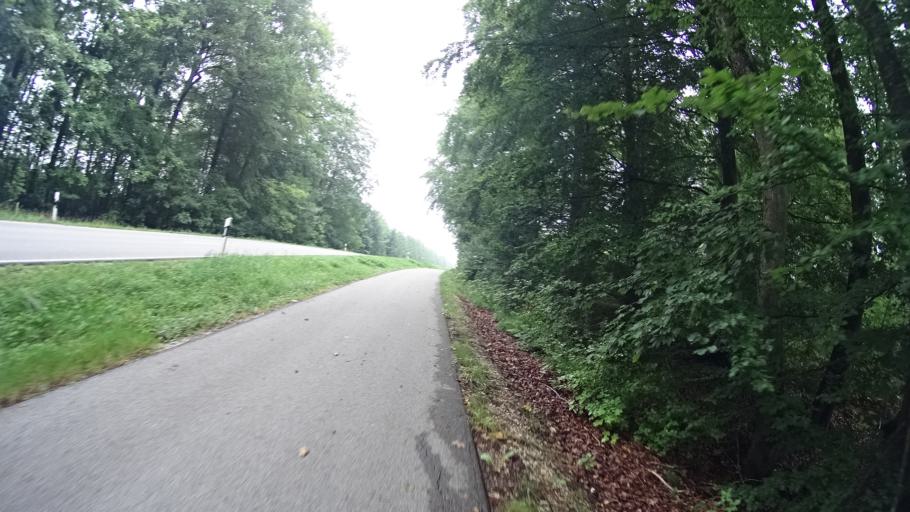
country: DE
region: Bavaria
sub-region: Upper Bavaria
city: Denkendorf
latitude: 48.9035
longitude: 11.4570
